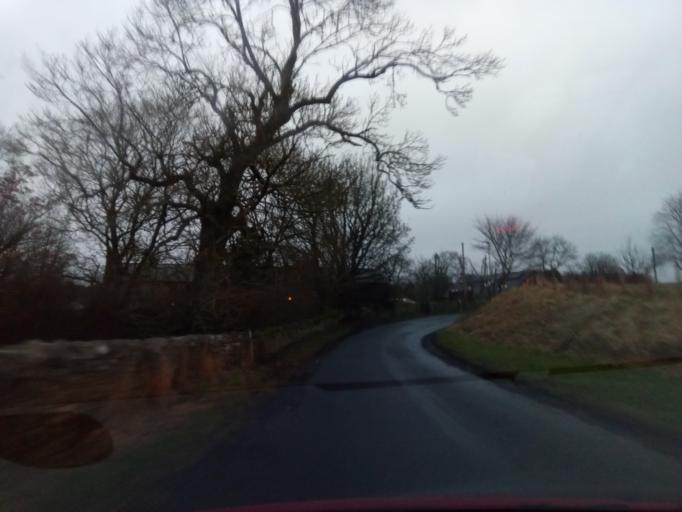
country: GB
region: England
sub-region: Northumberland
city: Otterburn
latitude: 55.2307
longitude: -2.1036
